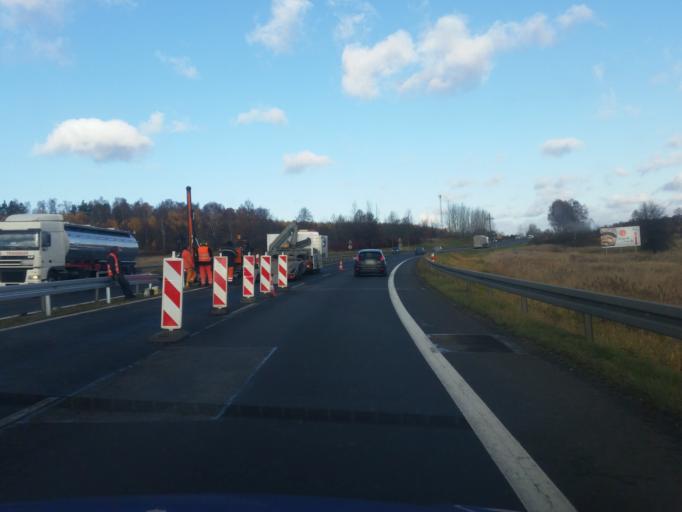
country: PL
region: Silesian Voivodeship
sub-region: Powiat czestochowski
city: Kamienica Polska
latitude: 50.6332
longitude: 19.1366
